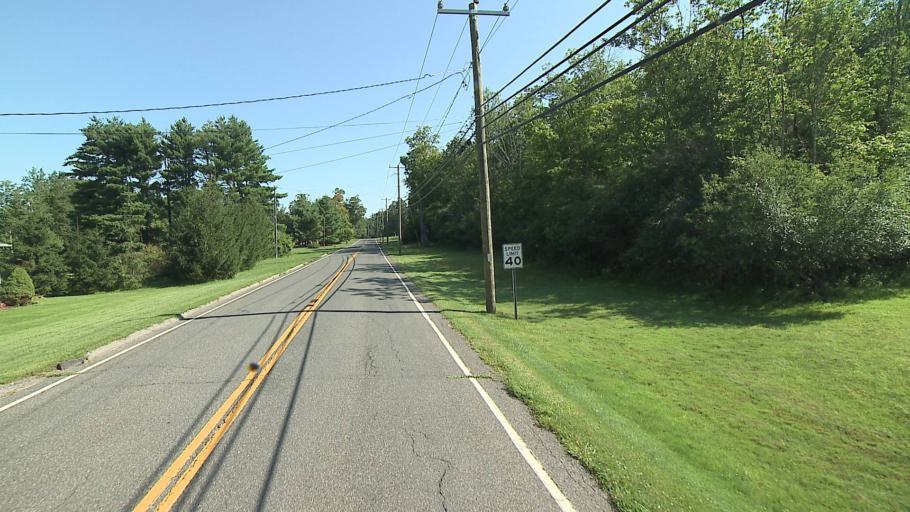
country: US
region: Connecticut
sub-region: Litchfield County
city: Kent
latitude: 41.8642
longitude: -73.4779
